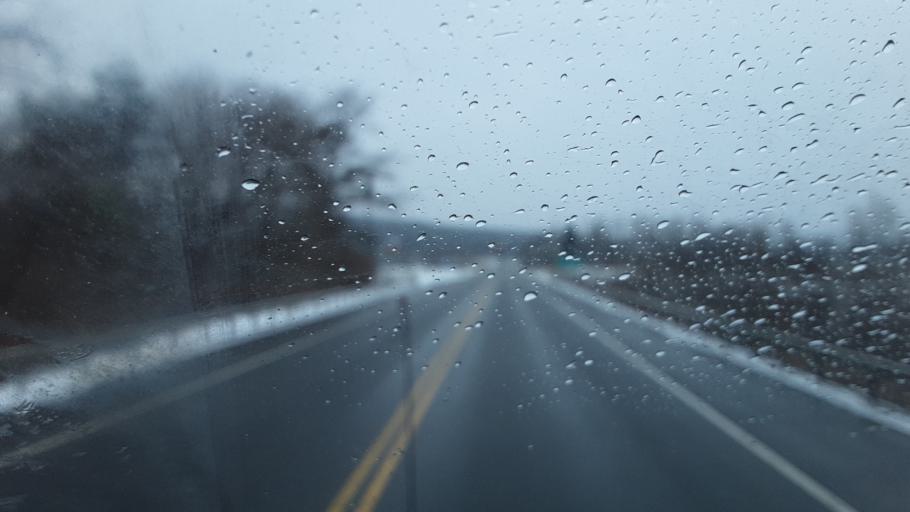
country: US
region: New York
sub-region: Allegany County
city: Belmont
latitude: 42.2531
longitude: -78.0588
